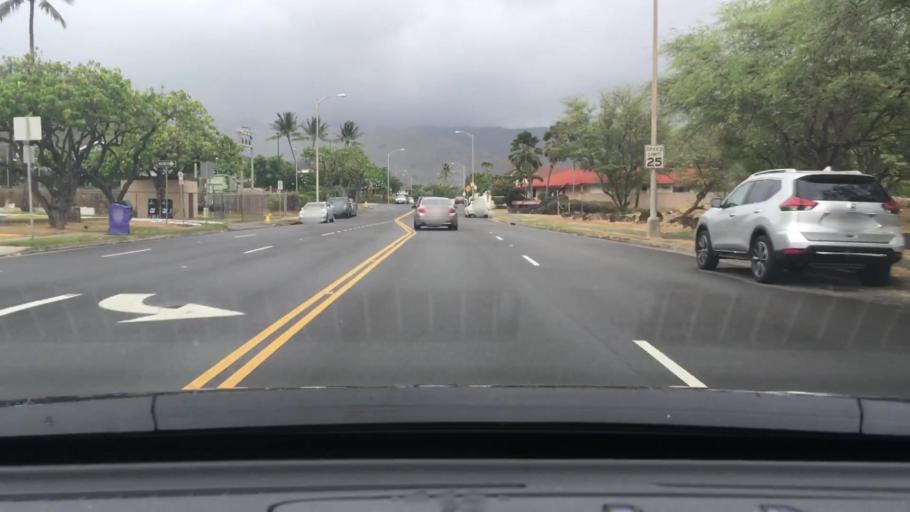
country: US
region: Hawaii
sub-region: Honolulu County
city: Waimanalo Beach
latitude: 21.2886
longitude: -157.7019
